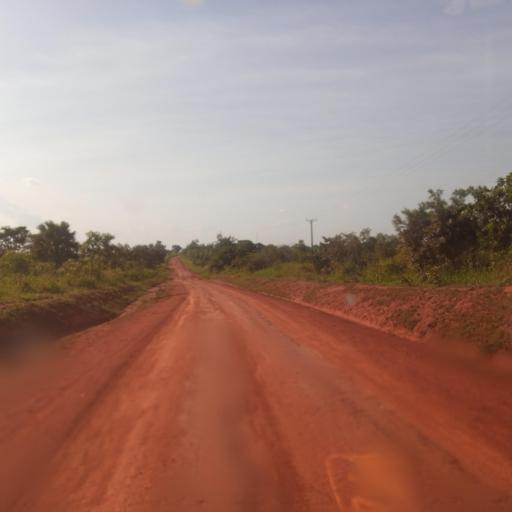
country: UG
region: Northern Region
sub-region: Kitgum District
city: Kitgum
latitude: 3.1138
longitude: 32.9148
